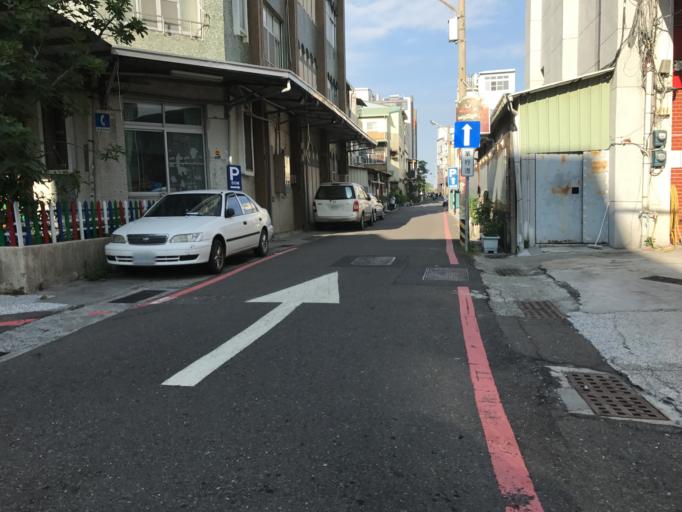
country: TW
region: Taiwan
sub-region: Tainan
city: Tainan
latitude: 23.0005
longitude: 120.1668
